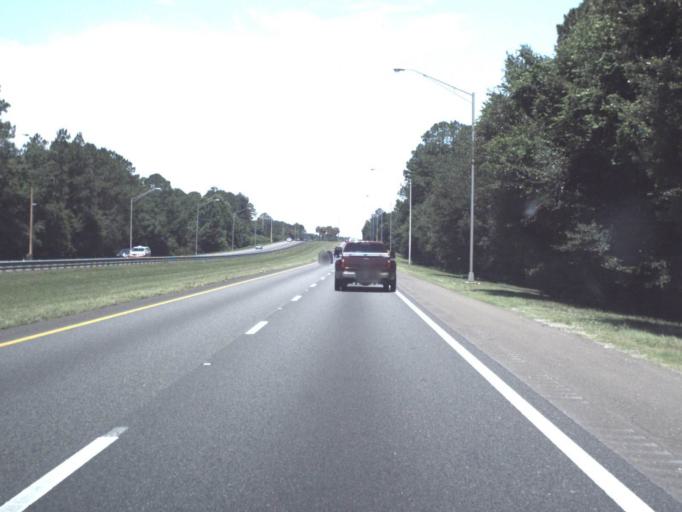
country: US
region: Florida
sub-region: Duval County
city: Jacksonville
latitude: 30.4434
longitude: -81.5953
